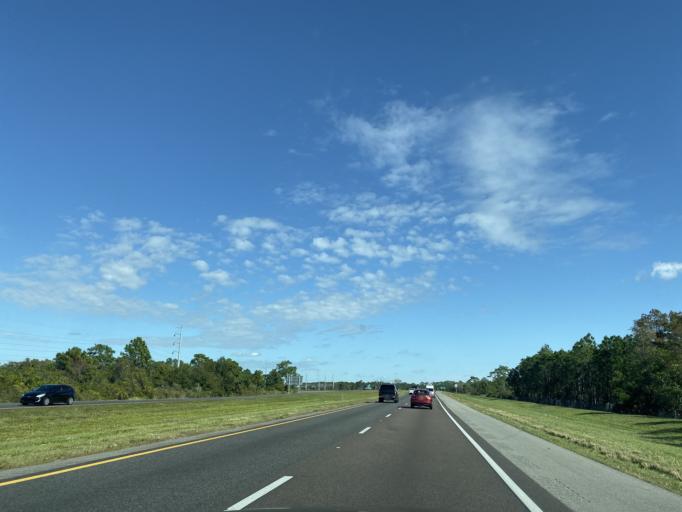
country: US
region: Florida
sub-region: Osceola County
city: Buenaventura Lakes
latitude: 28.3824
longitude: -81.2681
